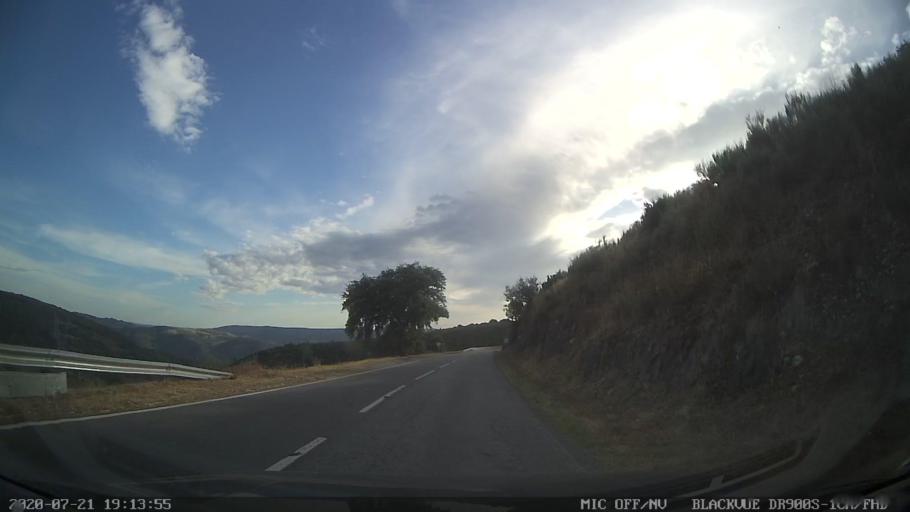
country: PT
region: Viseu
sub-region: Sao Joao da Pesqueira
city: Sao Joao da Pesqueira
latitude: 41.1572
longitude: -7.4513
